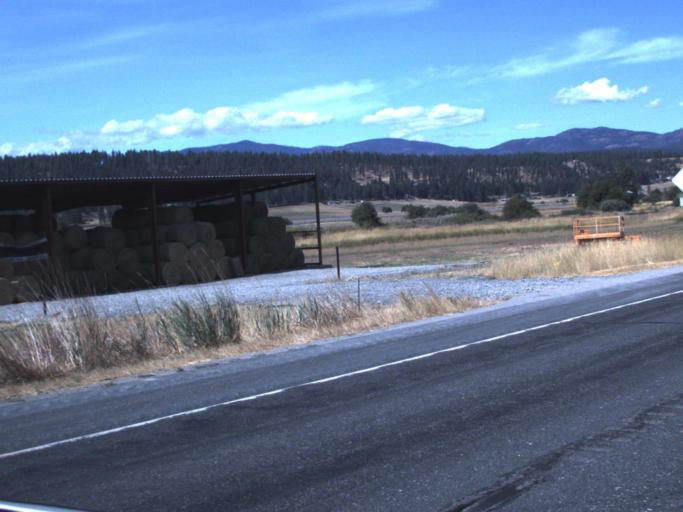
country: US
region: Washington
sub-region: Stevens County
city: Colville
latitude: 48.4388
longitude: -117.8653
